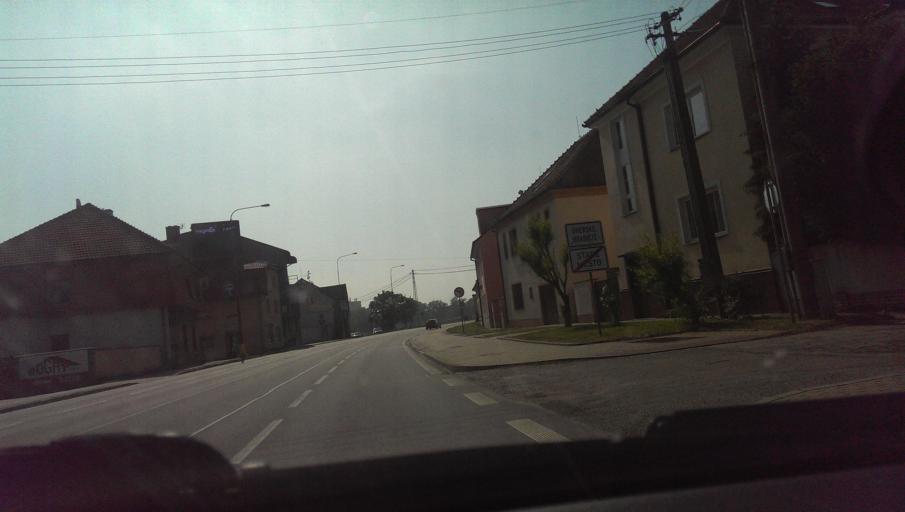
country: CZ
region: Zlin
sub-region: Okres Uherske Hradiste
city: Uherske Hradiste
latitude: 49.0745
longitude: 17.4572
